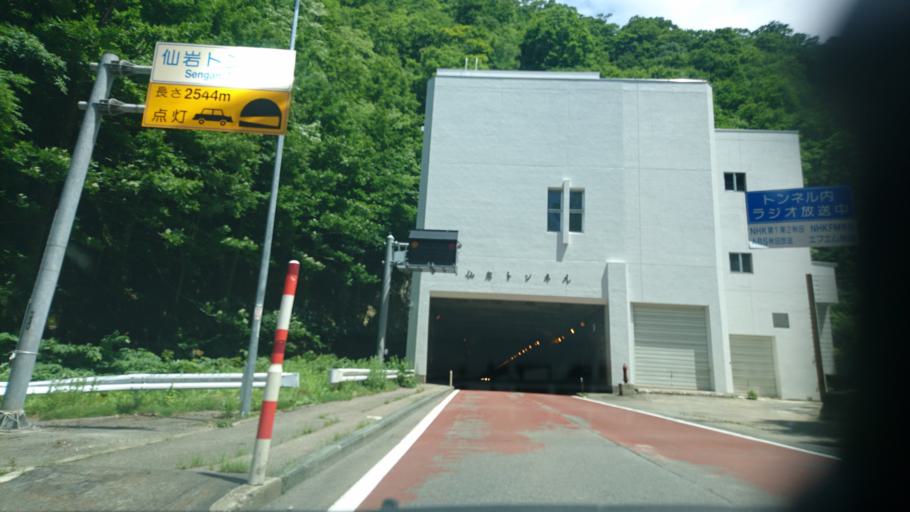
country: JP
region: Iwate
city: Shizukuishi
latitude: 39.6973
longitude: 140.8005
